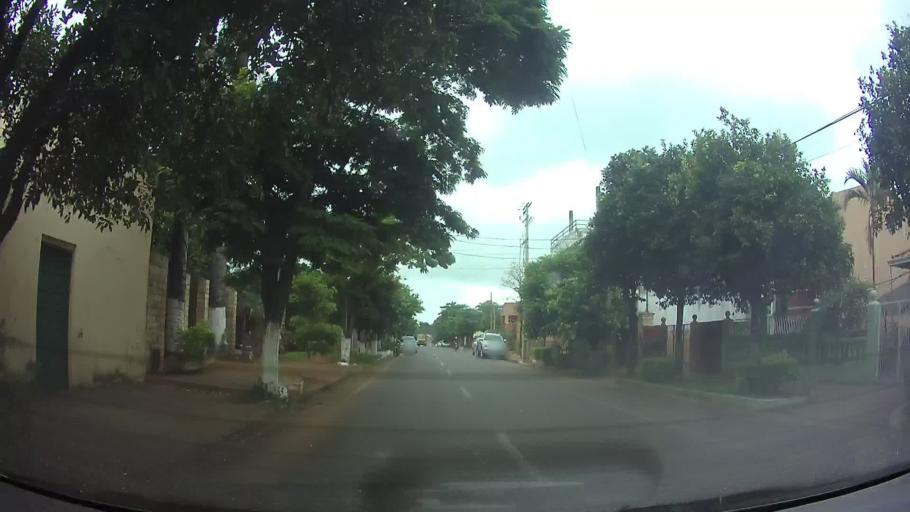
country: PY
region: Central
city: San Lorenzo
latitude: -25.2688
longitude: -57.4983
